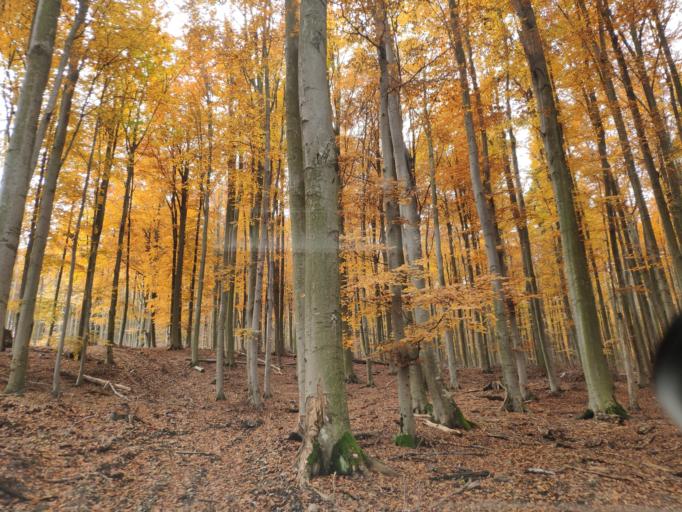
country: SK
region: Kosicky
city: Moldava nad Bodvou
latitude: 48.7352
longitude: 21.0142
